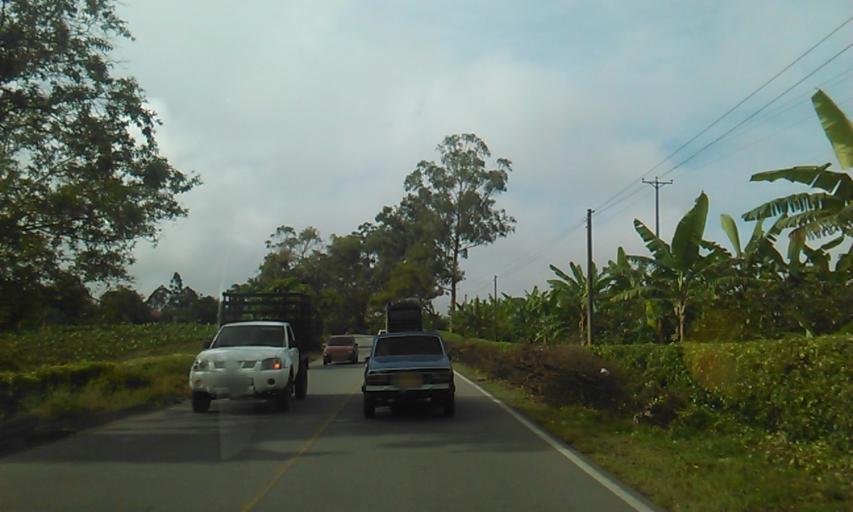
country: CO
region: Quindio
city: Cordoba
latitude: 4.4480
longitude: -75.7167
